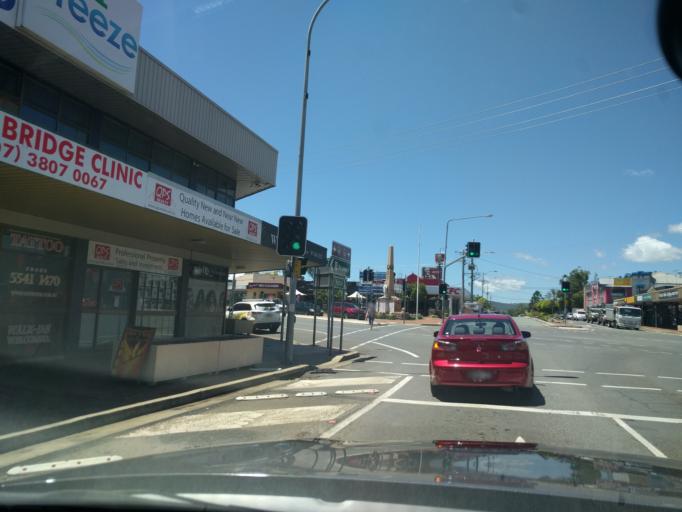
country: AU
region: Queensland
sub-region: Logan
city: Cedar Vale
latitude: -27.9880
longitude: 152.9959
